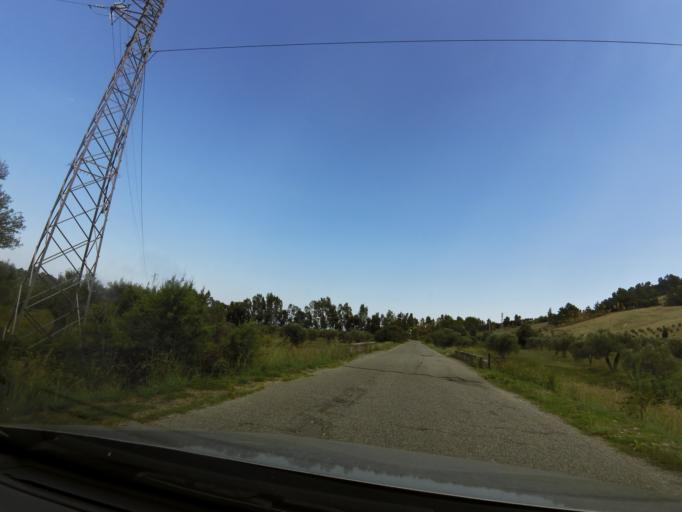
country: IT
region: Calabria
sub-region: Provincia di Reggio Calabria
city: Monasterace
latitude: 38.4264
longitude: 16.5321
